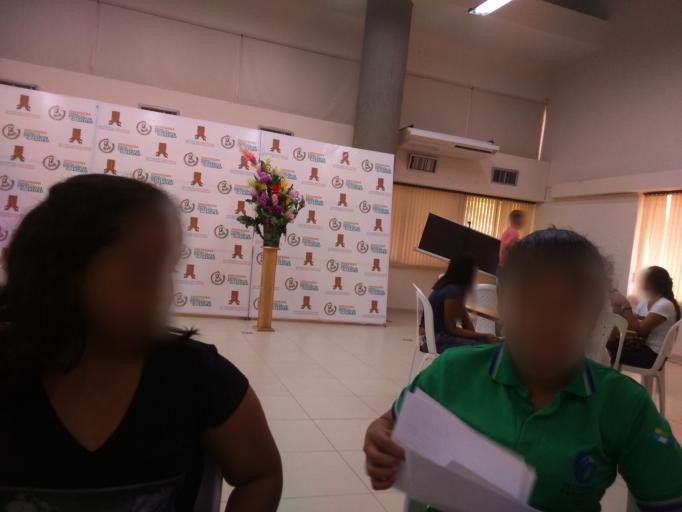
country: CO
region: La Guajira
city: Riohacha
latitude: 11.5133
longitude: -72.8697
